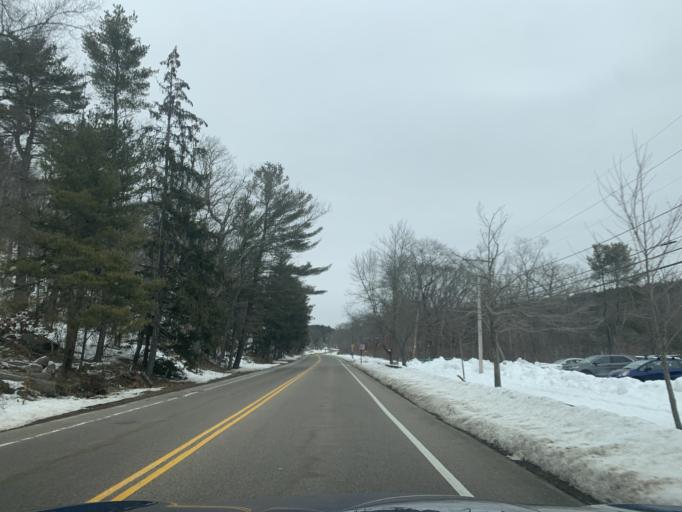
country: US
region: Massachusetts
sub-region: Norfolk County
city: Milton
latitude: 42.2102
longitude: -71.0966
